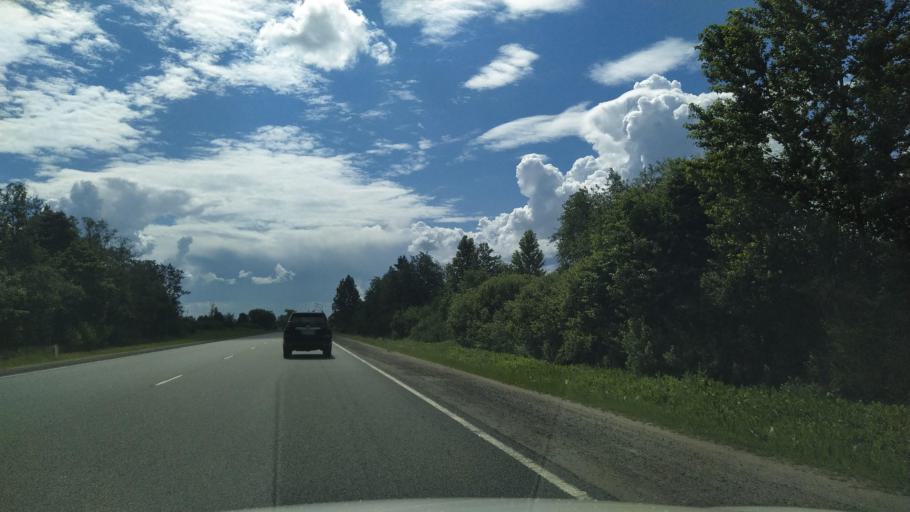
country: RU
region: Leningrad
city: Rozhdestveno
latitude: 59.3578
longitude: 29.9623
